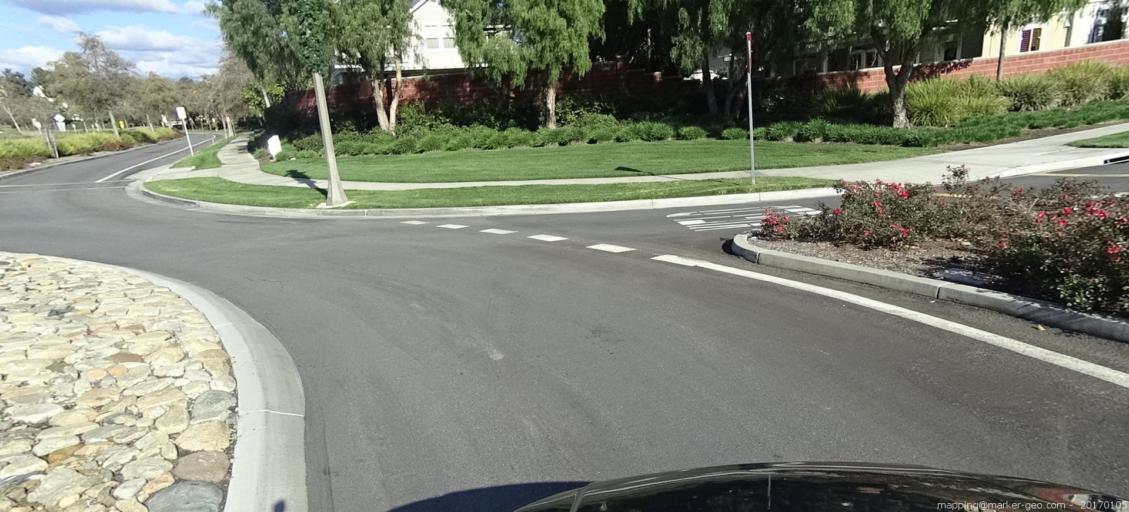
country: US
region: California
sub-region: Orange County
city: Ladera Ranch
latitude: 33.5550
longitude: -117.6371
